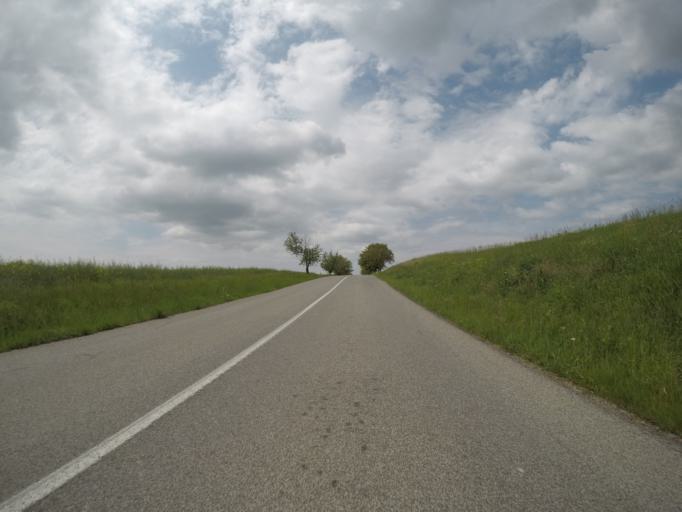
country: SK
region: Banskobystricky
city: Dudince
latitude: 48.0789
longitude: 18.8192
